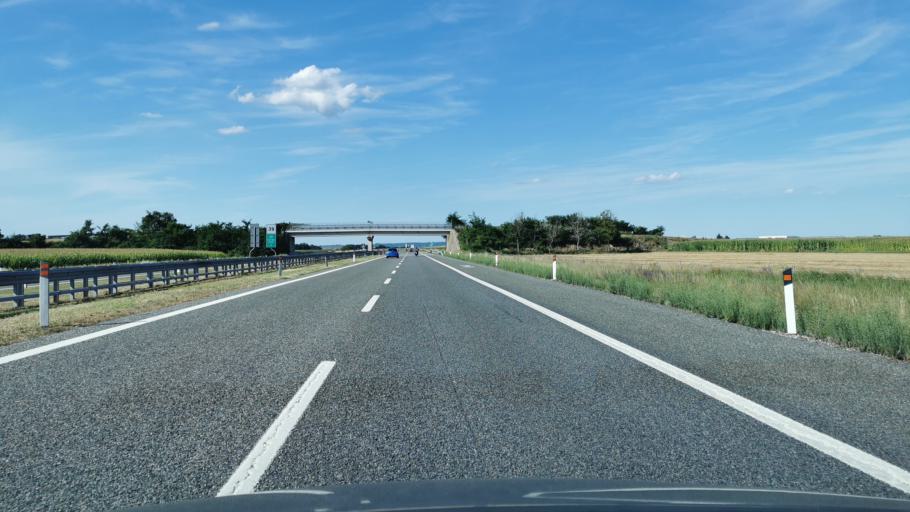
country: IT
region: Piedmont
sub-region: Provincia di Cuneo
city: Cervere
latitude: 44.6230
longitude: 7.7720
